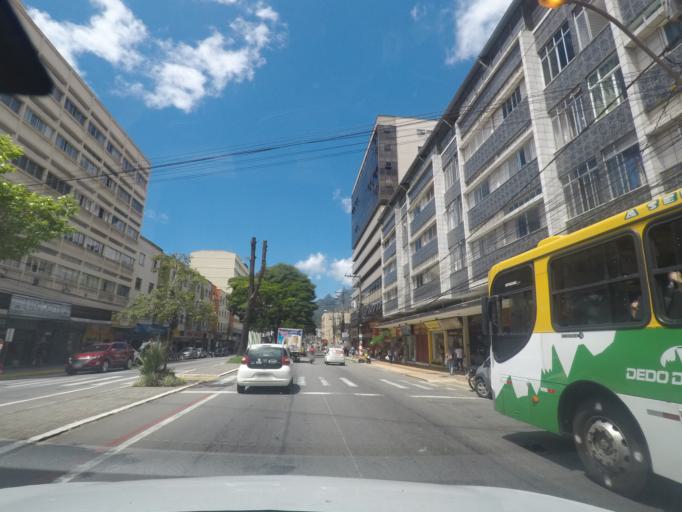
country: BR
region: Rio de Janeiro
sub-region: Teresopolis
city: Teresopolis
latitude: -22.4145
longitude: -42.9708
